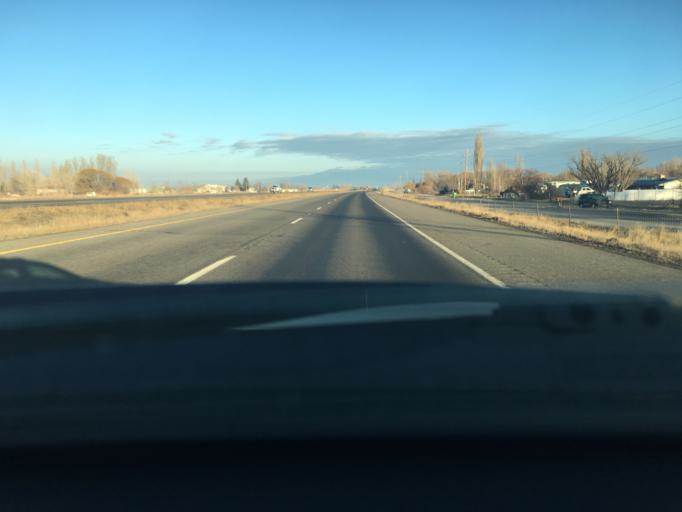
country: US
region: Colorado
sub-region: Montrose County
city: Olathe
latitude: 38.5524
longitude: -107.9496
